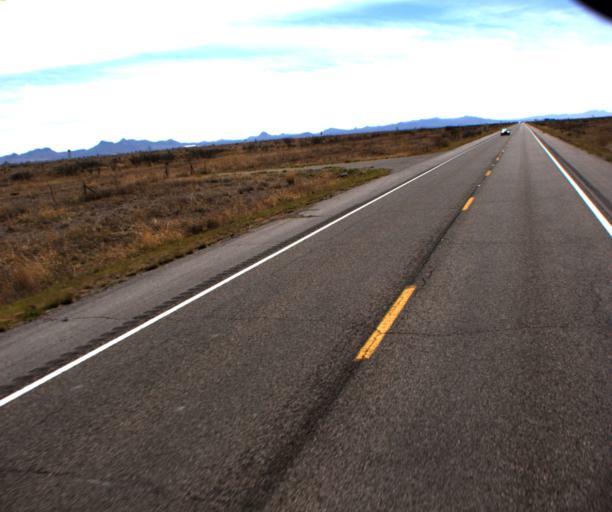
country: US
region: Arizona
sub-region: Cochise County
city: Pirtleville
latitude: 31.4737
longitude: -109.6207
